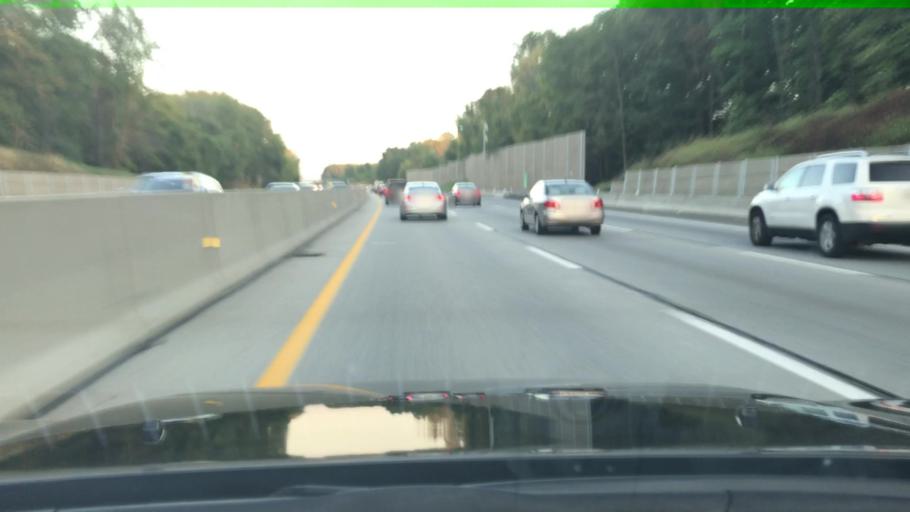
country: US
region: Pennsylvania
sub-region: Bucks County
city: Feasterville
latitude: 40.1545
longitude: -75.0321
